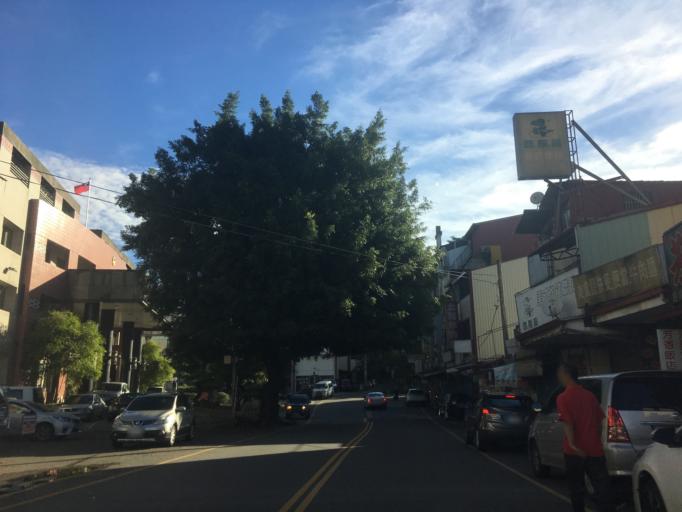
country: TW
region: Taiwan
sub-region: Nantou
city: Puli
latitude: 24.0228
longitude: 121.1324
